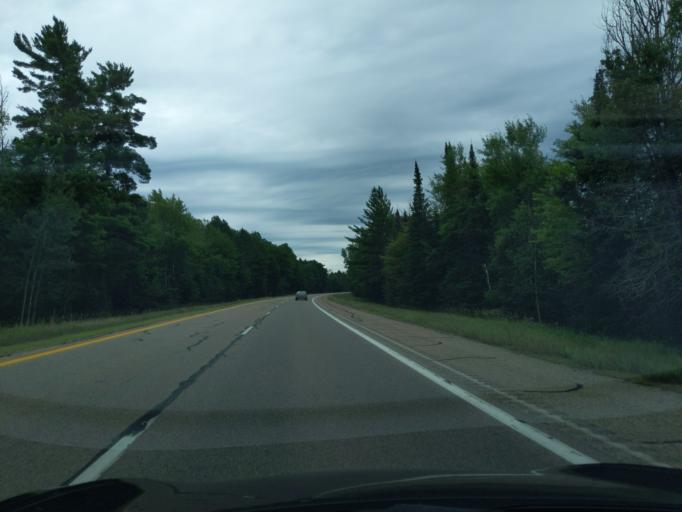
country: US
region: Michigan
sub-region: Roscommon County
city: Houghton Lake
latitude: 44.2265
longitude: -84.7980
